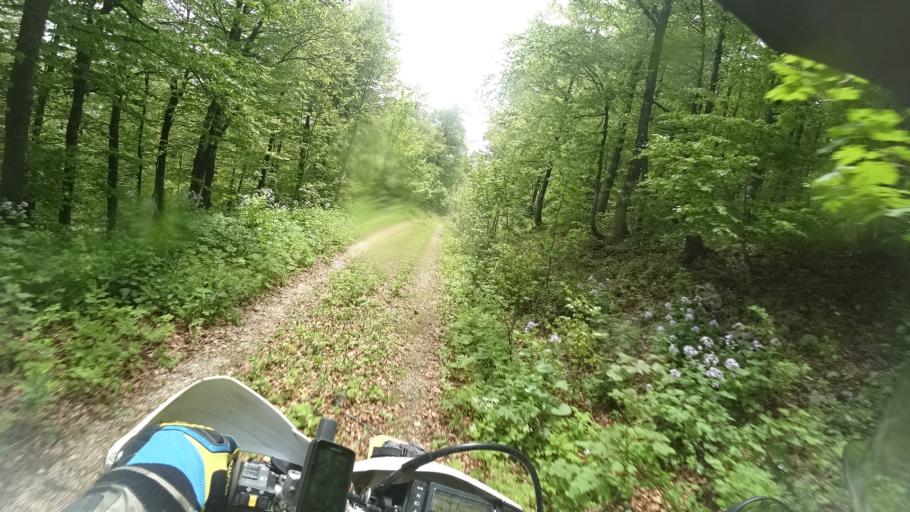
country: BA
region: Federation of Bosnia and Herzegovina
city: Orasac
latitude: 44.5685
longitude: 15.8790
